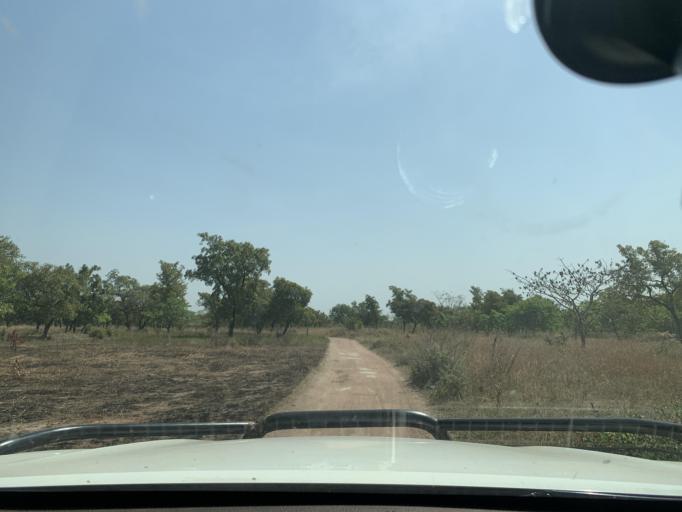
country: ML
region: Sikasso
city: Kolondieba
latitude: 10.8394
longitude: -6.8002
